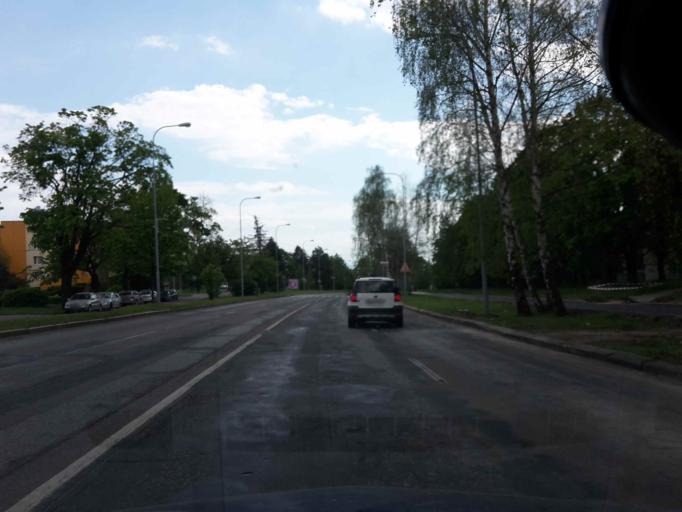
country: CZ
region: South Moravian
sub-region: Mesto Brno
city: Brno
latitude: 49.2294
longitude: 16.6311
